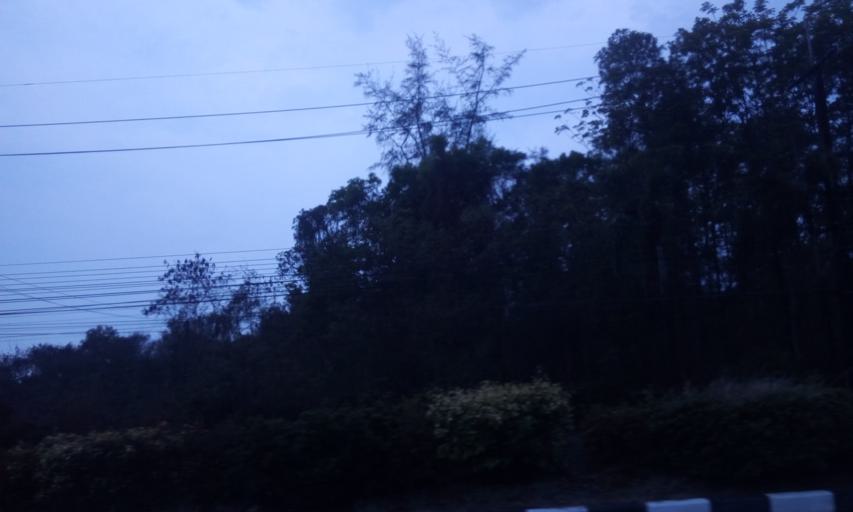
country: TH
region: Trat
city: Khao Saming
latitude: 12.3838
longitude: 102.3722
